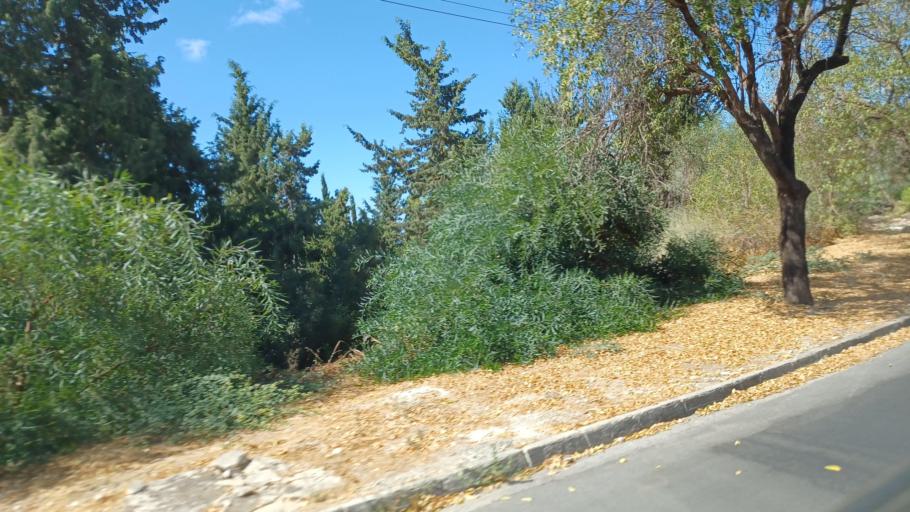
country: CY
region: Pafos
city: Tala
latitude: 34.8478
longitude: 32.4324
